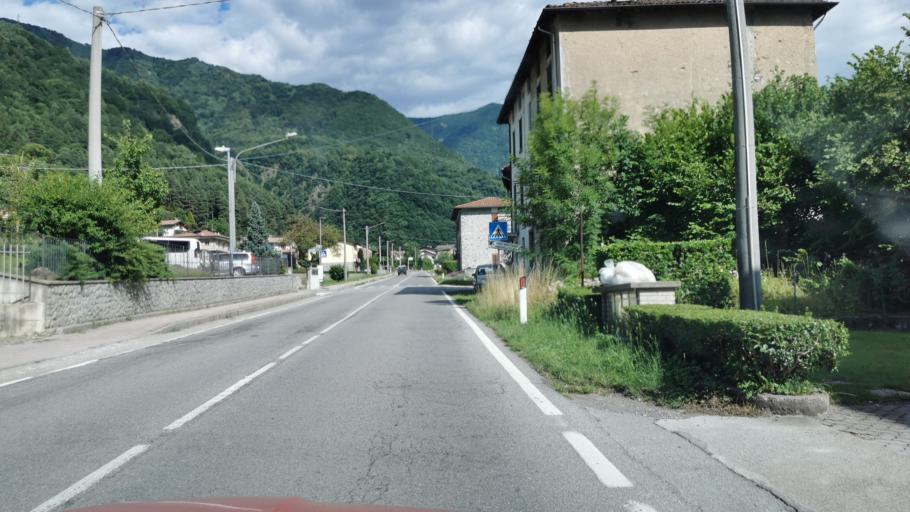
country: IT
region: Lombardy
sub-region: Provincia di Lecco
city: Primaluna
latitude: 45.9808
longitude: 9.4426
